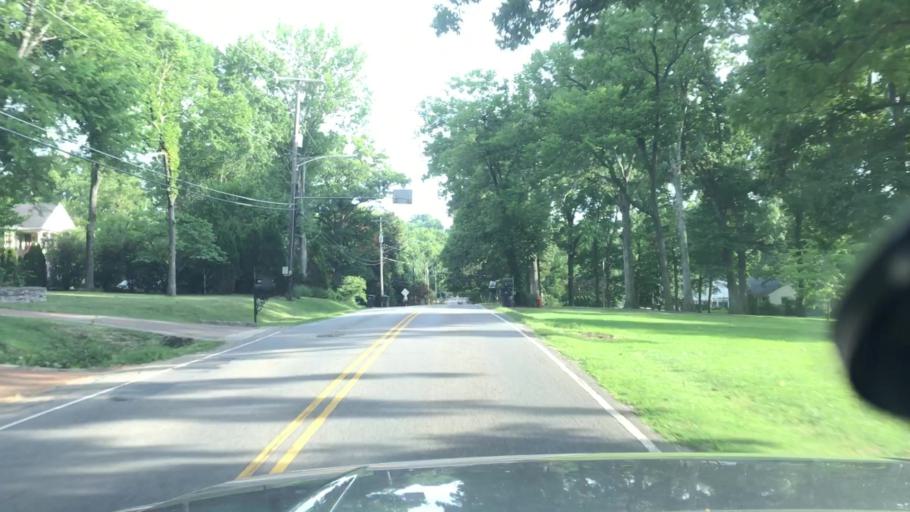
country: US
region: Tennessee
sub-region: Davidson County
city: Belle Meade
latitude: 36.0985
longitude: -86.8389
